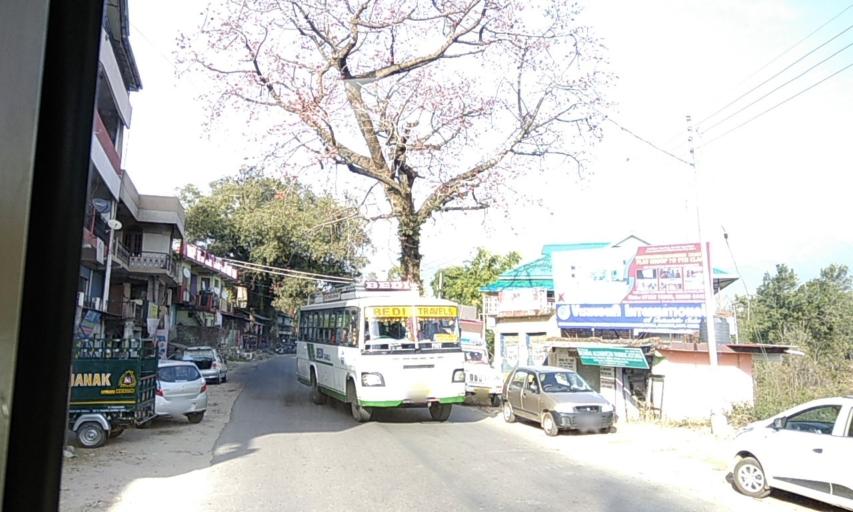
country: IN
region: Himachal Pradesh
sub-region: Kangra
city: Palampur
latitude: 32.0838
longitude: 76.5229
